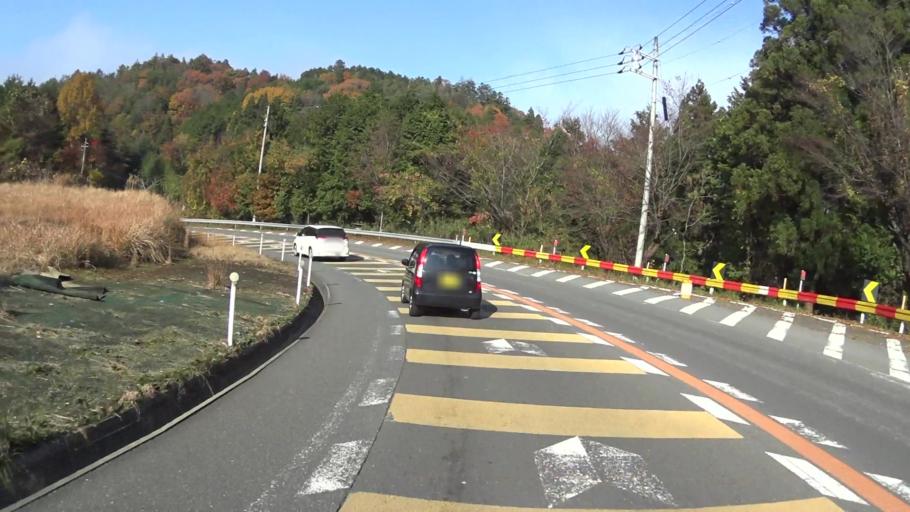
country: JP
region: Kyoto
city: Fukuchiyama
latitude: 35.2679
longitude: 135.1460
